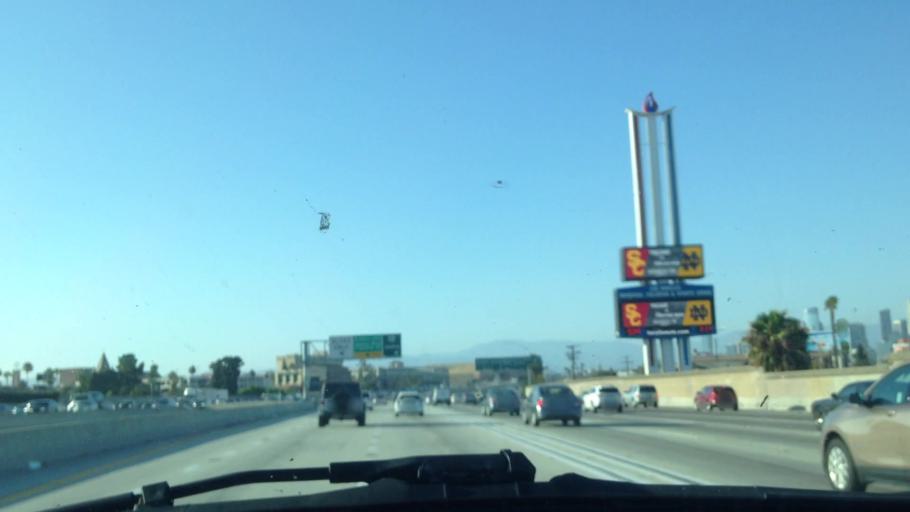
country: US
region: California
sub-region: Los Angeles County
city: Los Angeles
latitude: 34.0128
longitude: -118.2808
